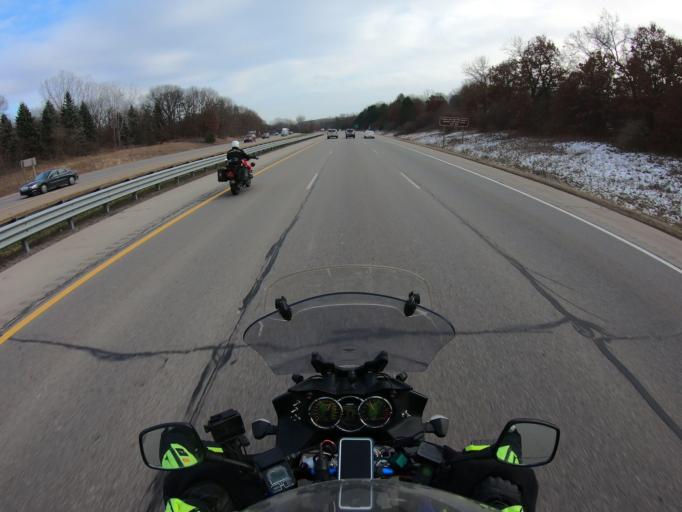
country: US
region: Michigan
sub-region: Oakland County
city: Clarkston
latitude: 42.7423
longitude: -83.4741
